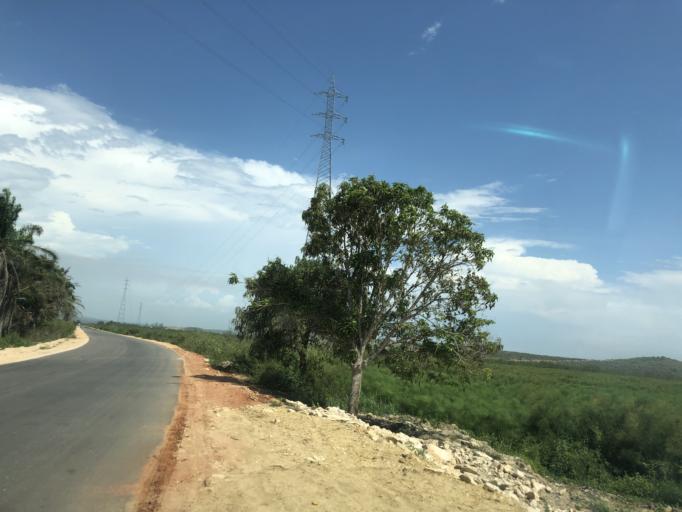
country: AO
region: Cuanza Sul
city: Sumbe
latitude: -10.8813
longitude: 13.8413
